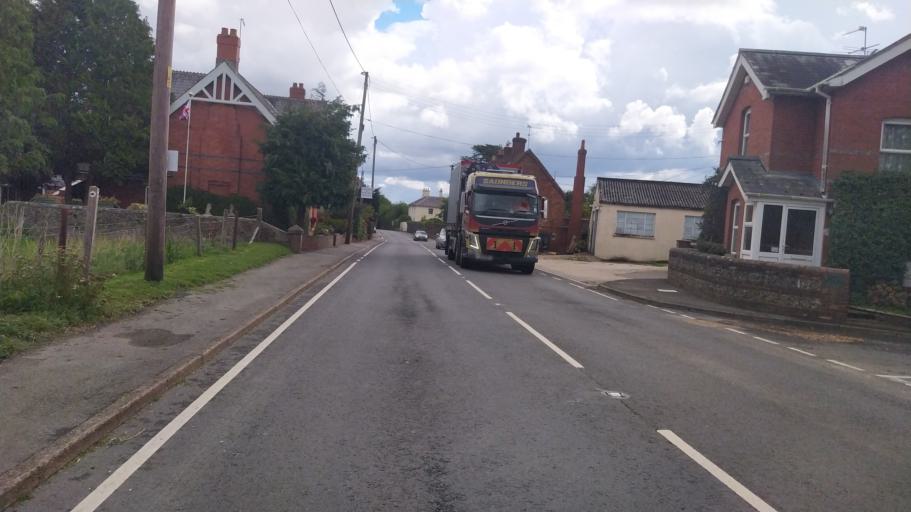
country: GB
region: England
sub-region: Dorset
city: Blandford Forum
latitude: 50.8780
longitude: -2.2030
